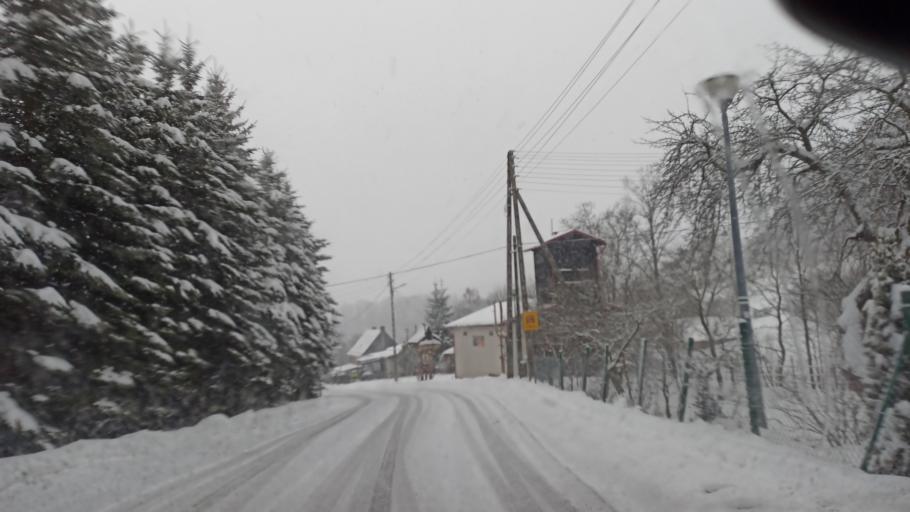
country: PL
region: Lower Silesian Voivodeship
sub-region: Powiat klodzki
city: Ludwikowice Klodzkie
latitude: 50.6547
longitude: 16.4730
